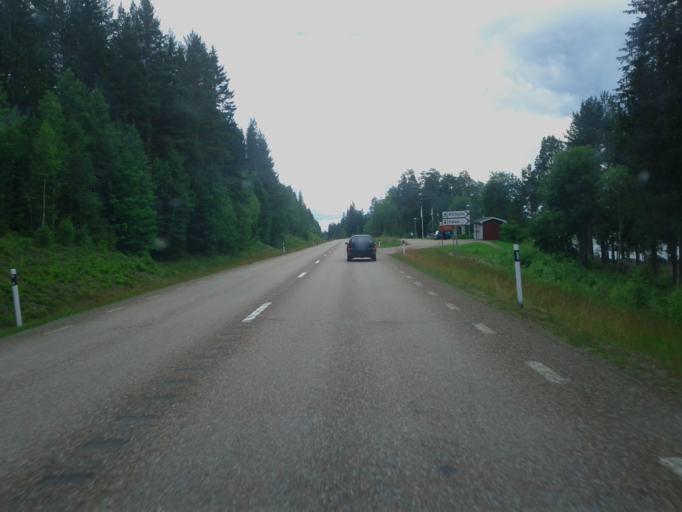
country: SE
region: Dalarna
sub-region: Faluns Kommun
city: Bjursas
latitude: 60.7742
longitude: 15.3167
